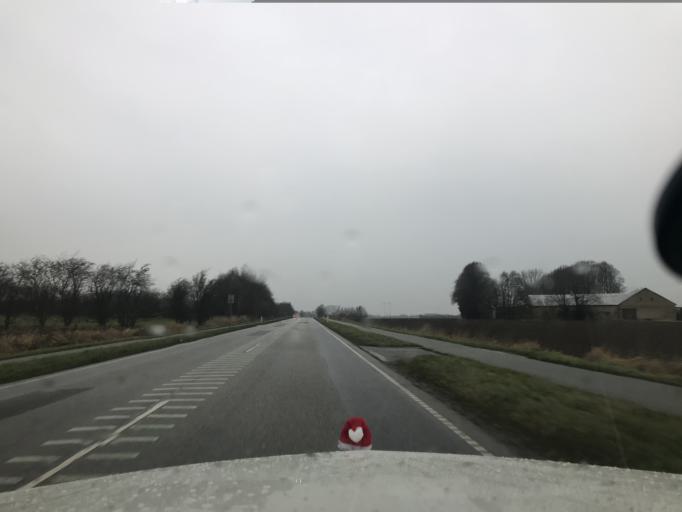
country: DK
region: South Denmark
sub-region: Sonderborg Kommune
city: Dybbol
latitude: 54.9486
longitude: 9.7110
